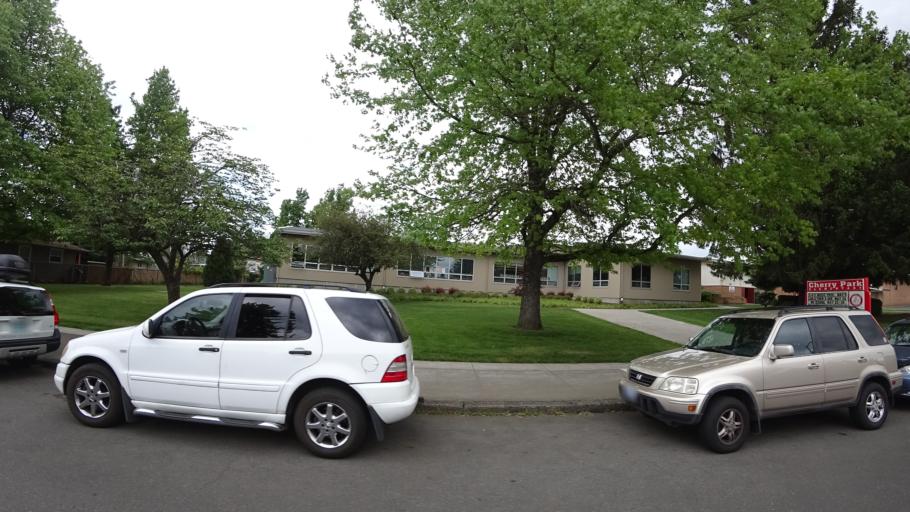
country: US
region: Oregon
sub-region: Multnomah County
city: Lents
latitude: 45.5094
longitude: -122.5564
